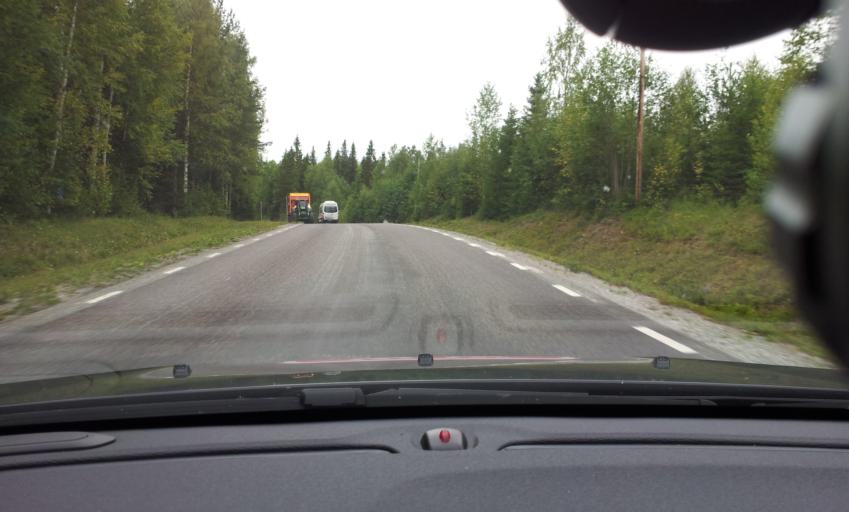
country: SE
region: Jaemtland
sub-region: Braecke Kommun
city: Braecke
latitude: 63.0137
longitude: 15.2006
